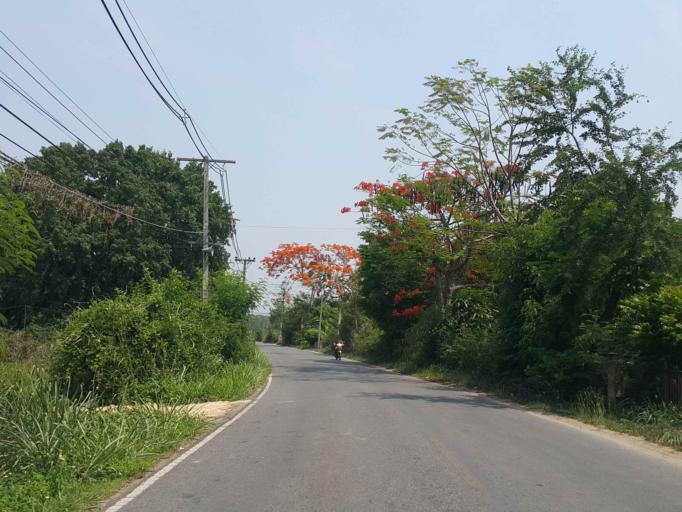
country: TH
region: Chiang Mai
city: San Sai
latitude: 18.8813
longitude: 98.9799
